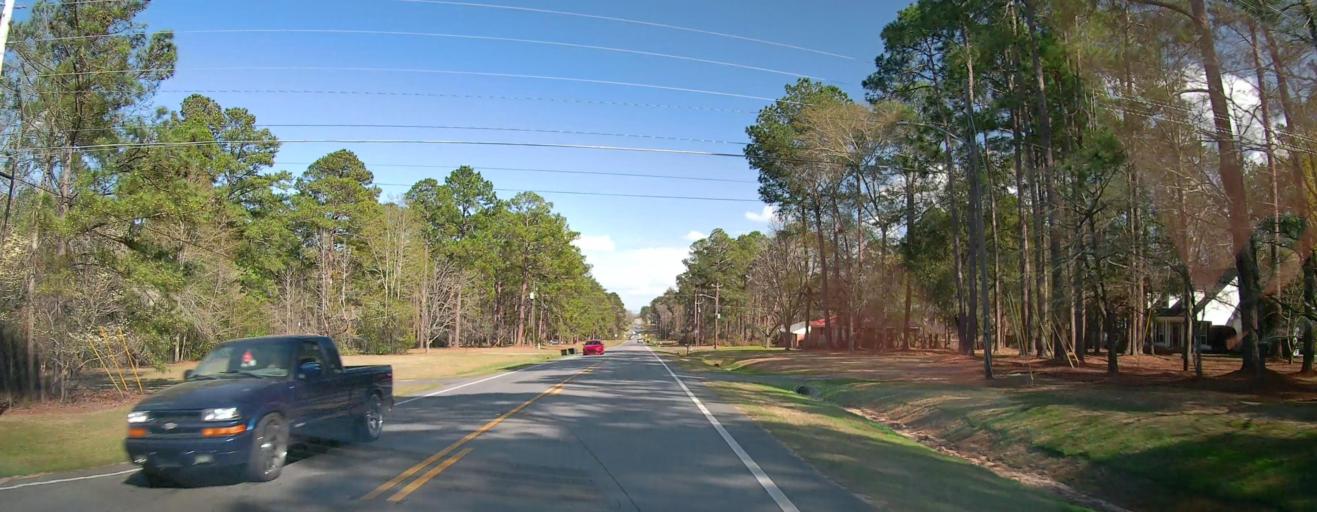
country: US
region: Georgia
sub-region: Dodge County
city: Eastman
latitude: 32.1968
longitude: -83.2021
